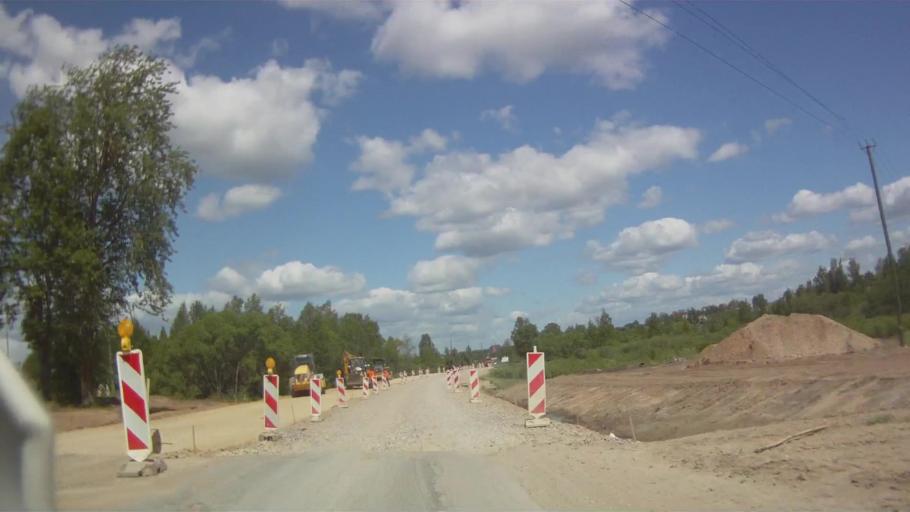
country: LV
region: Rezekne
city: Rezekne
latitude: 56.4899
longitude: 27.3141
